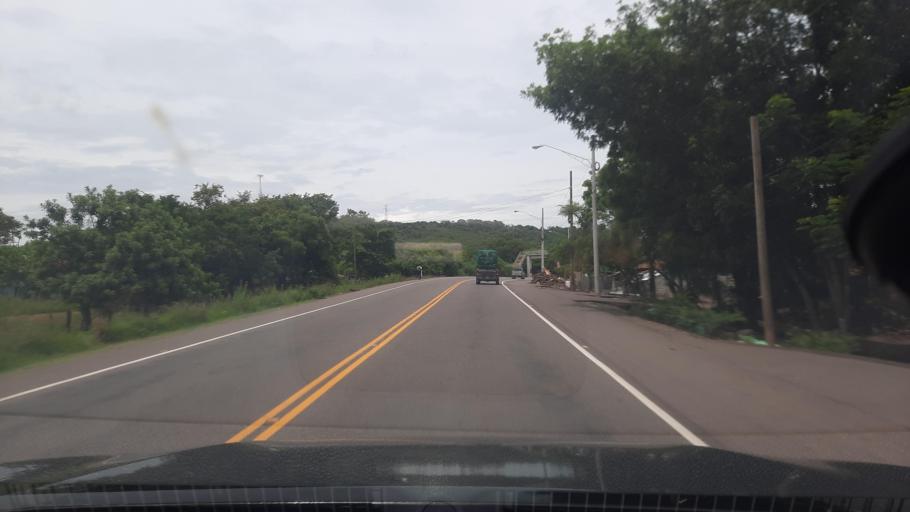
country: HN
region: Valle
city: Goascoran
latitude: 13.5572
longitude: -87.6522
